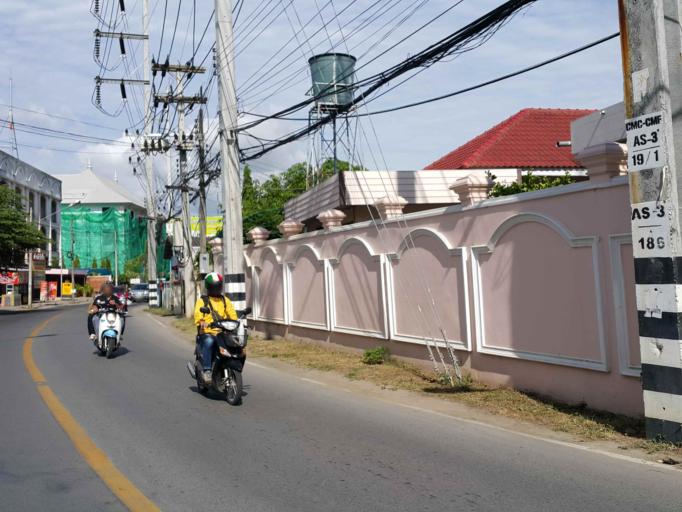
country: TH
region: Chiang Mai
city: Chiang Mai
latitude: 18.7623
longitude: 99.0015
